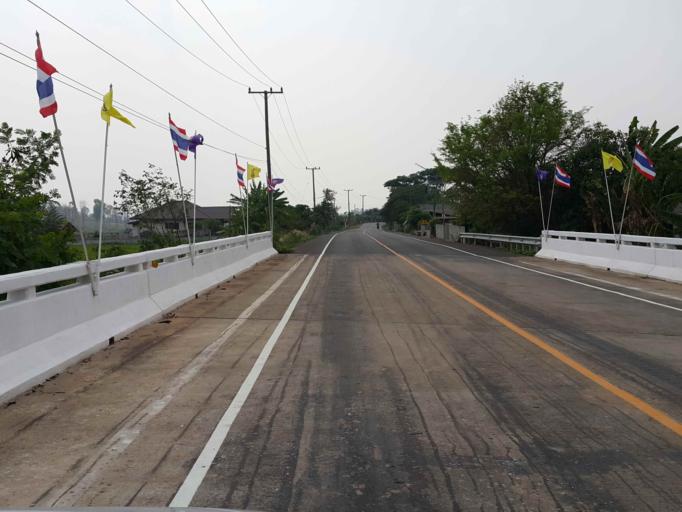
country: TH
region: Chiang Mai
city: Mae Taeng
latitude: 19.1121
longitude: 99.0778
